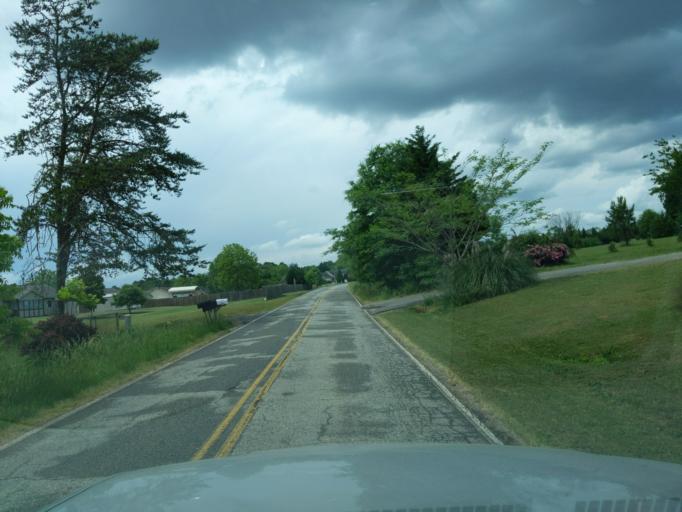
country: US
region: South Carolina
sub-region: Spartanburg County
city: Inman Mills
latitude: 35.0134
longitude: -82.1219
